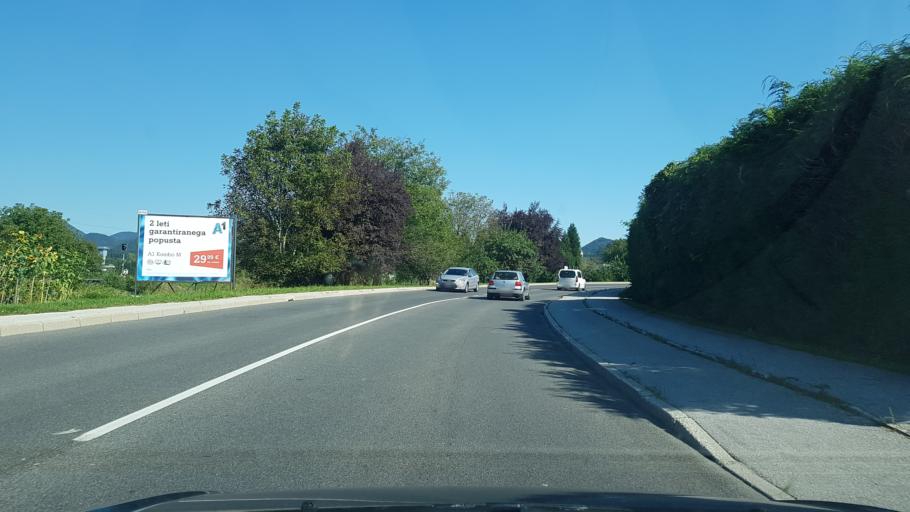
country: SI
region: Velenje
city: Velenje
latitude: 46.3674
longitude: 15.0870
